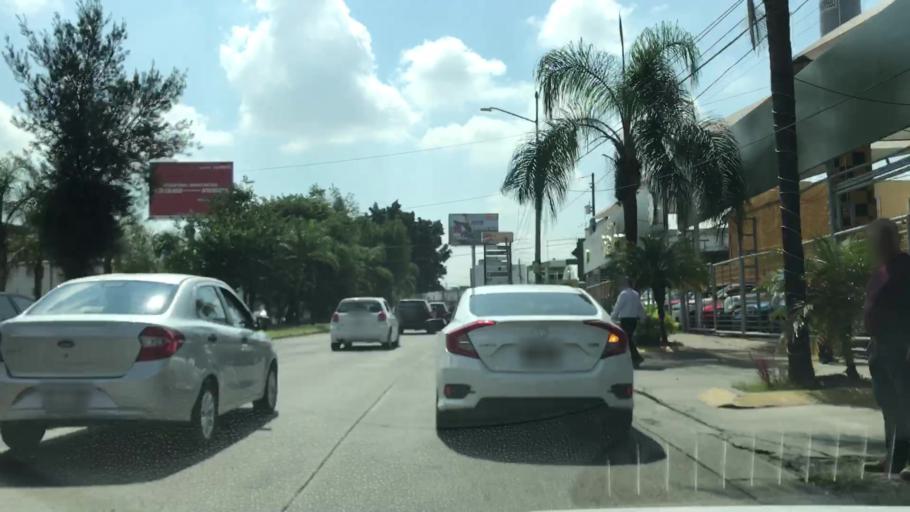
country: MX
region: Jalisco
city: Guadalajara
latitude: 20.6406
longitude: -103.4199
